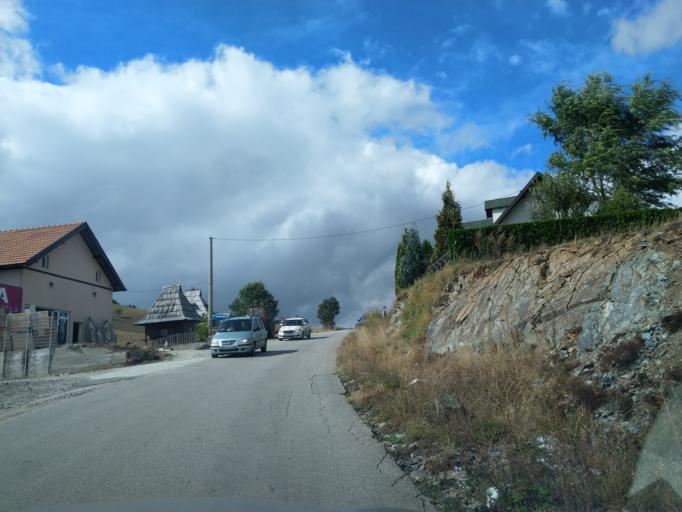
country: RS
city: Zlatibor
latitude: 43.7196
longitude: 19.7311
